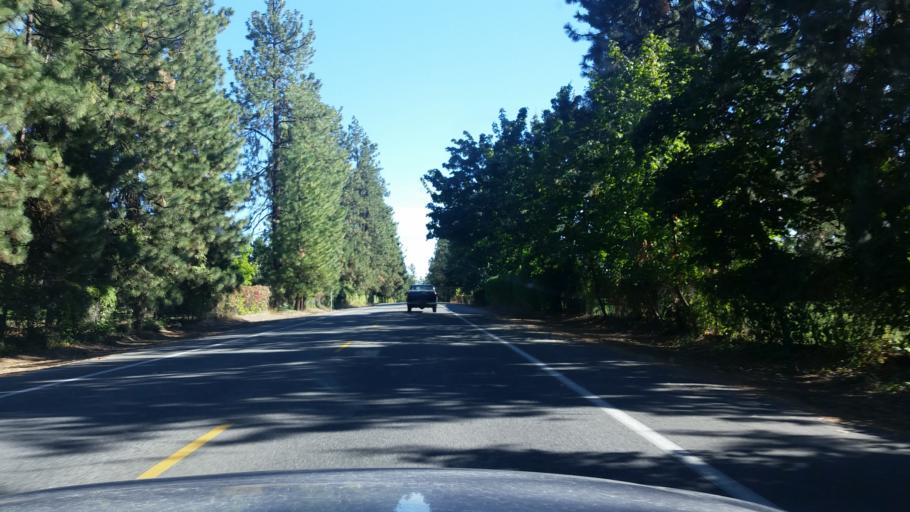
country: US
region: Washington
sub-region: Spokane County
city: Spokane
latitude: 47.6106
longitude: -117.3977
